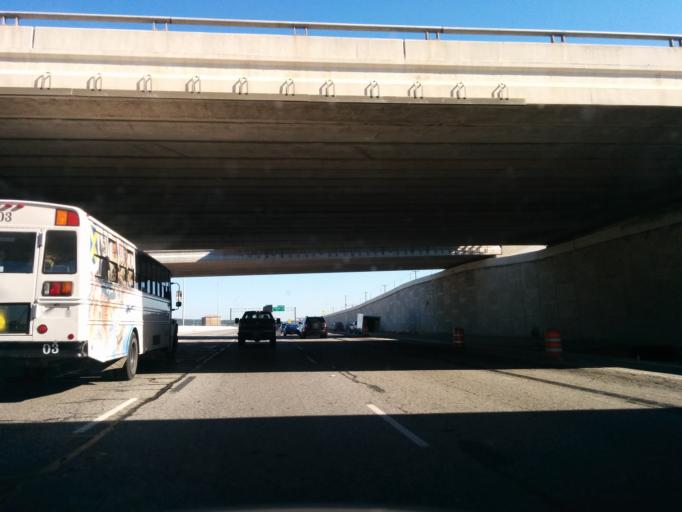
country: US
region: Texas
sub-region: Bexar County
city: Shavano Park
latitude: 29.5753
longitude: -98.5946
